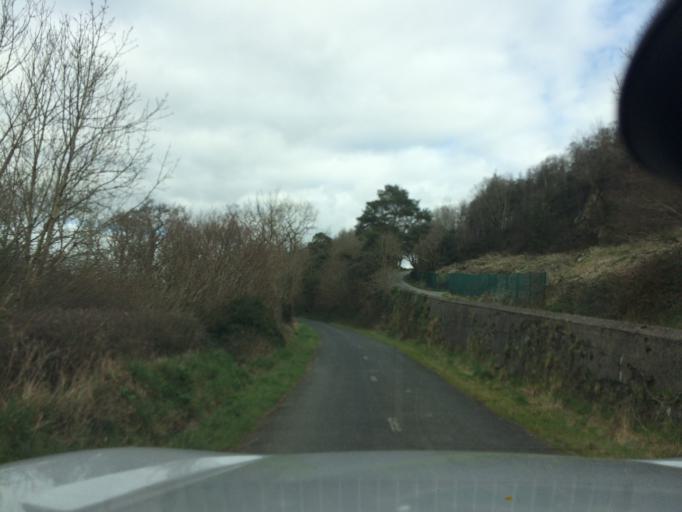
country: IE
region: Munster
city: Carrick-on-Suir
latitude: 52.2822
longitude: -7.4102
